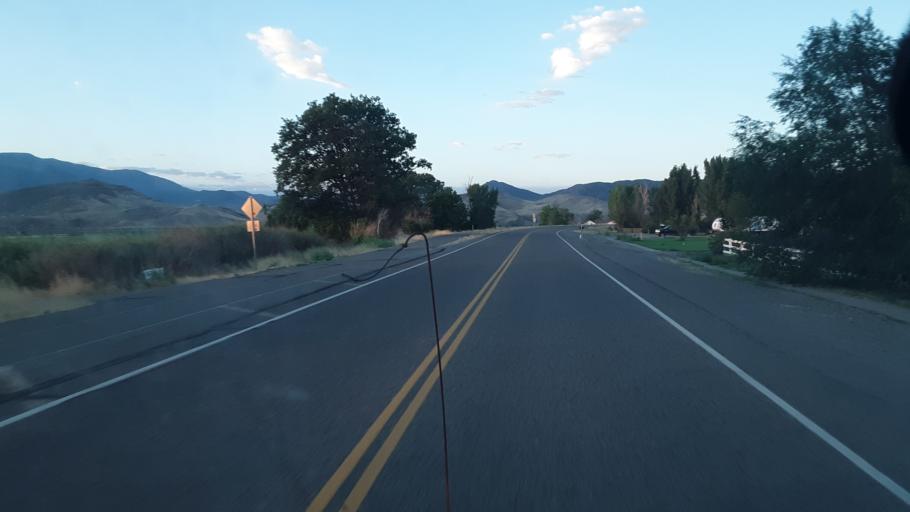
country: US
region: Utah
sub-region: Sevier County
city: Monroe
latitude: 38.6212
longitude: -112.2185
